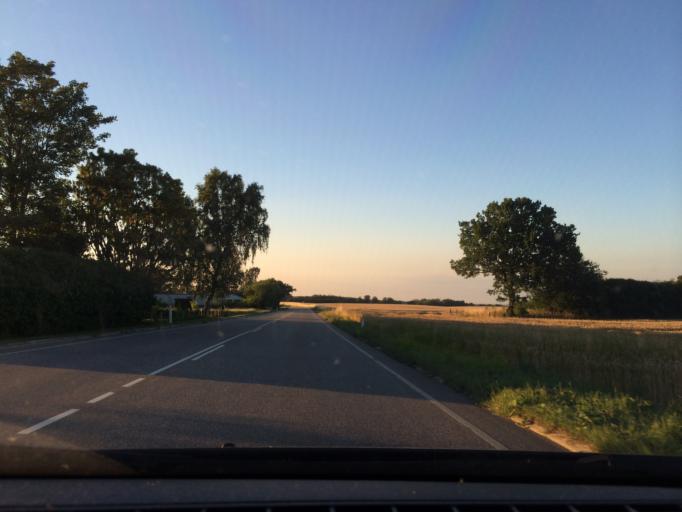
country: DK
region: Zealand
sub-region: Vordingborg Kommune
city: Praesto
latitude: 55.0826
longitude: 12.0823
